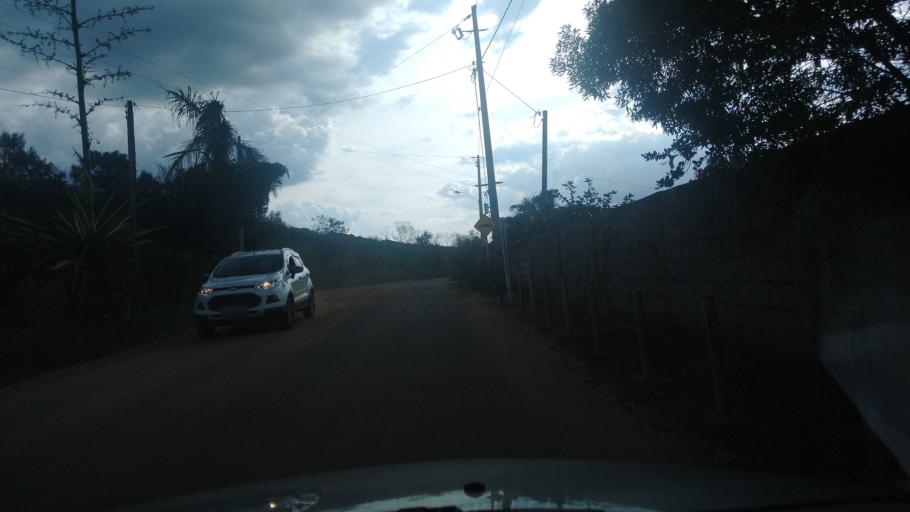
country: BR
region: Minas Gerais
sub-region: Extrema
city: Extrema
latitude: -22.7248
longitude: -46.3499
